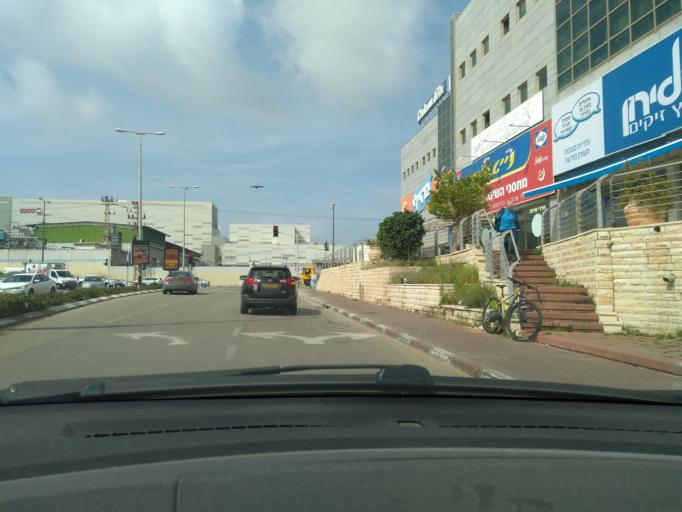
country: IL
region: Central District
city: Even Yehuda
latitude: 32.2749
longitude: 34.8599
